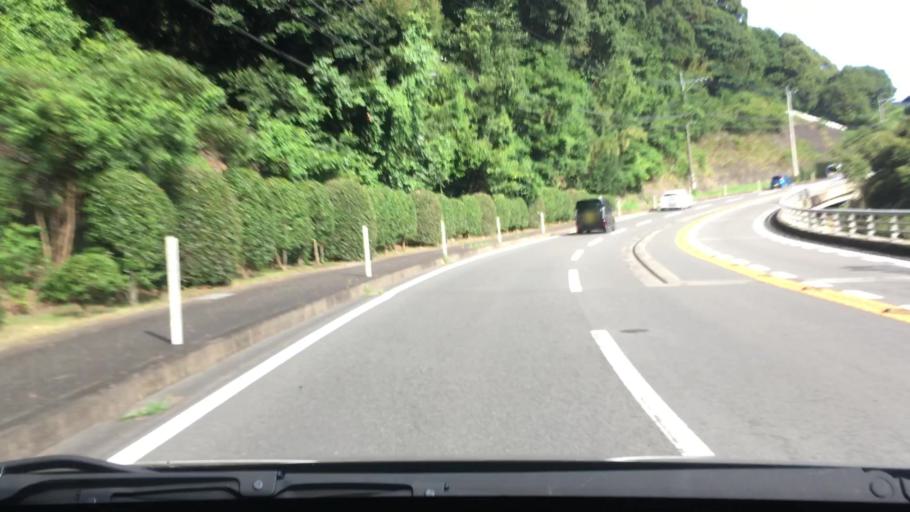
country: JP
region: Nagasaki
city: Togitsu
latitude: 32.8219
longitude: 129.7995
